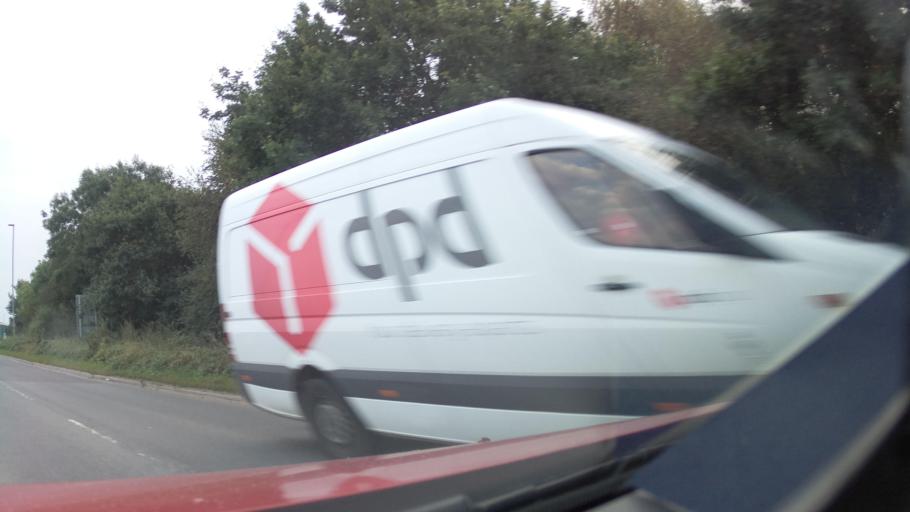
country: GB
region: England
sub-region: Lincolnshire
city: Skellingthorpe
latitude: 53.1546
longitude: -0.6719
